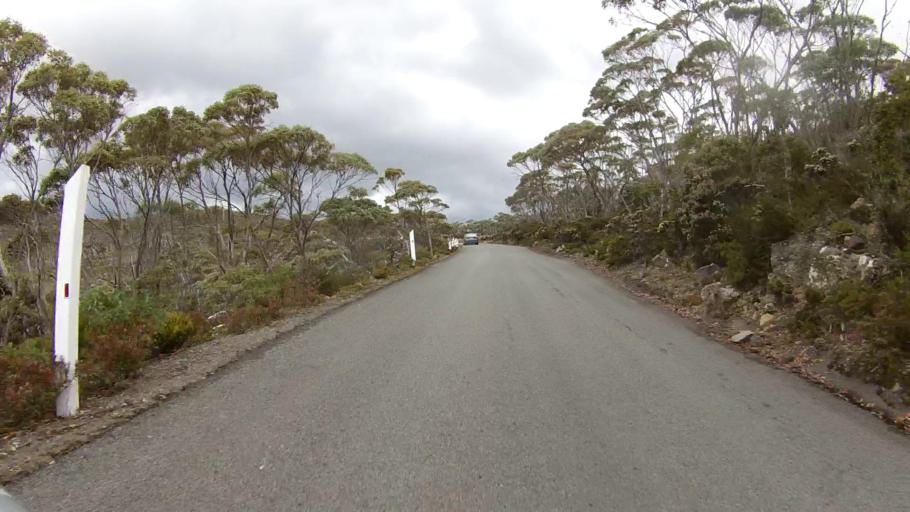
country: AU
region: Tasmania
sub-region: Glenorchy
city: West Moonah
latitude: -42.8881
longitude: 147.2208
